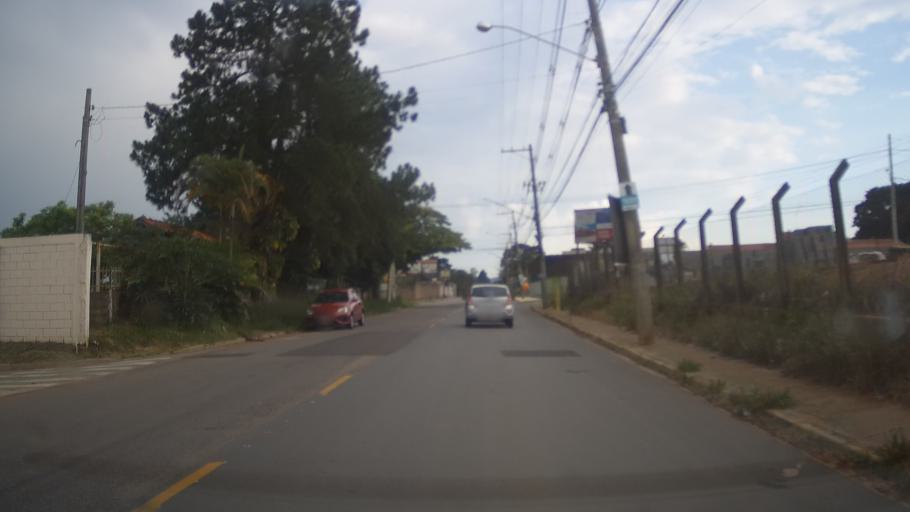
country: BR
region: Sao Paulo
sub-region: Itupeva
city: Itupeva
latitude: -23.1754
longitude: -46.9997
